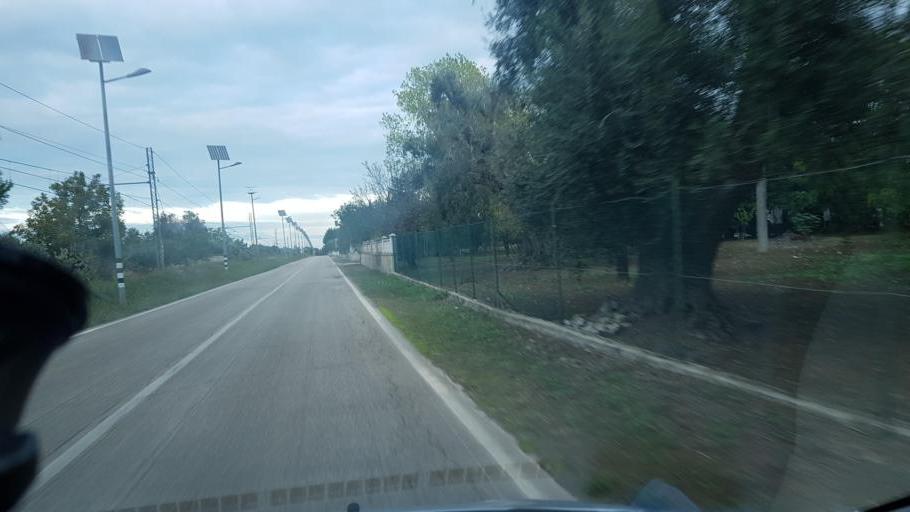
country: IT
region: Apulia
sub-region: Provincia di Brindisi
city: Latiano
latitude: 40.5399
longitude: 17.6944
